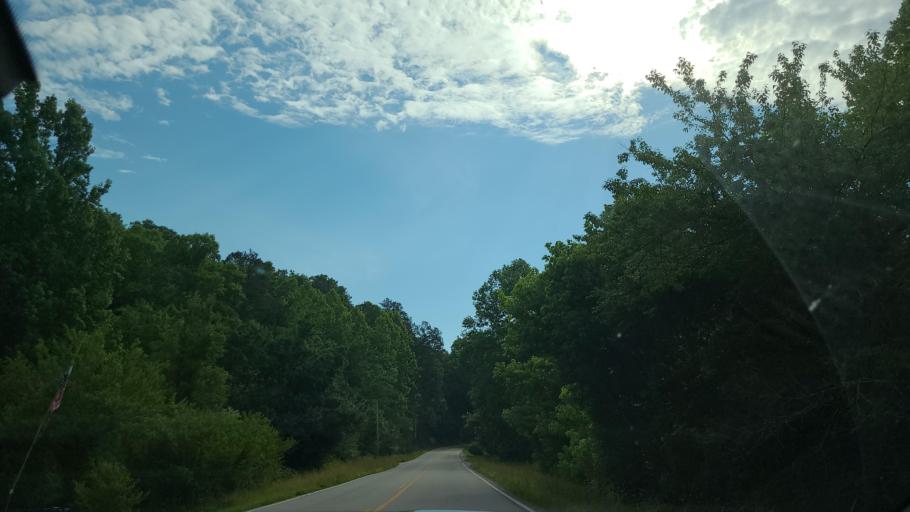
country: US
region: Kentucky
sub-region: Knox County
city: Barbourville
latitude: 36.6810
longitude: -83.9268
